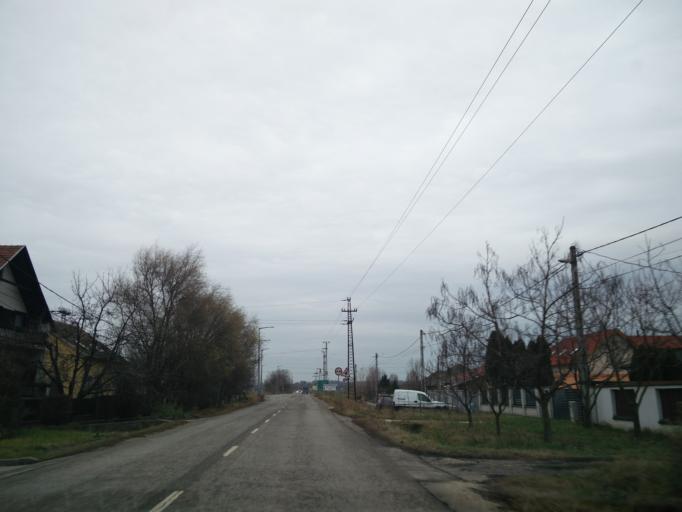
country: HU
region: Pest
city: Ullo
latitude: 47.3914
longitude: 19.3636
